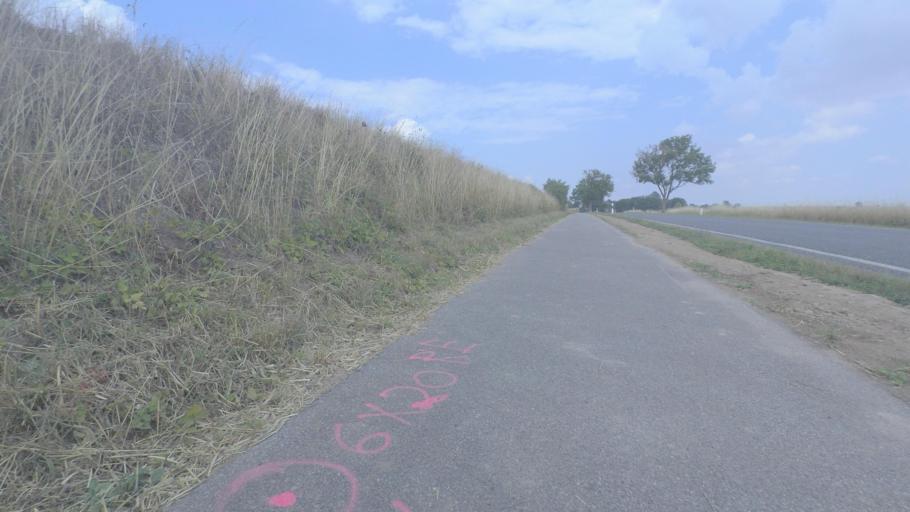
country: DE
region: Mecklenburg-Vorpommern
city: Borrentin
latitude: 53.8044
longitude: 12.9090
